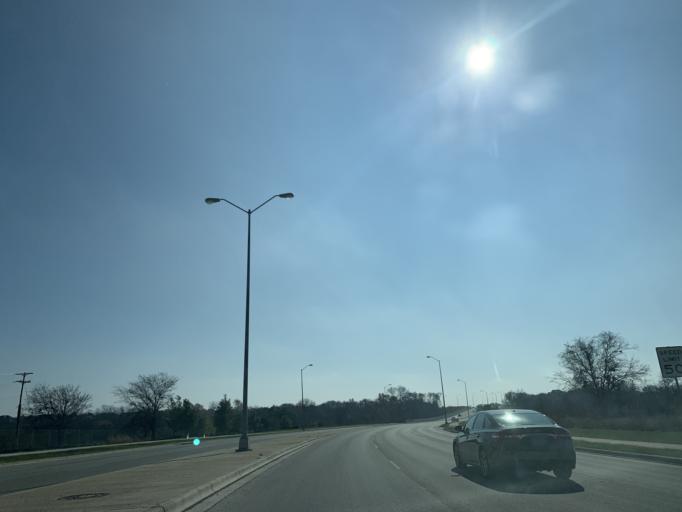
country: US
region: Texas
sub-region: Williamson County
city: Round Rock
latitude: 30.5165
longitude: -97.6371
